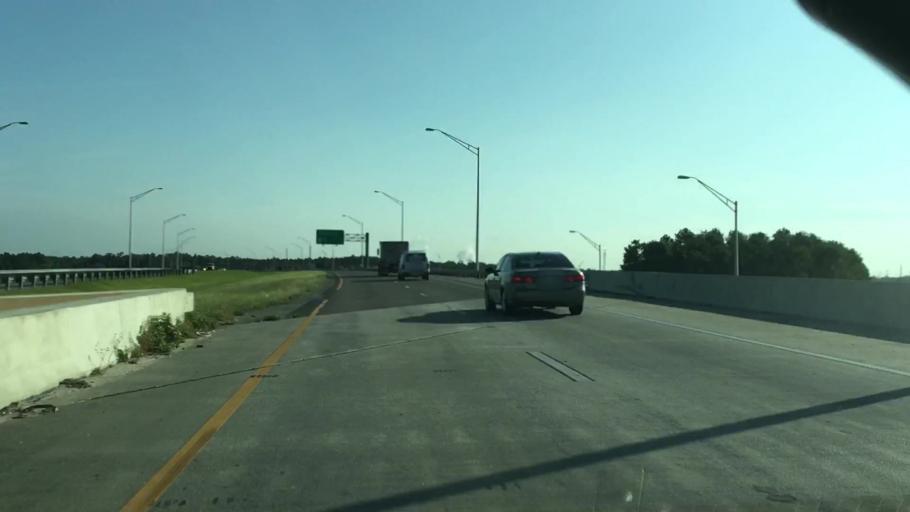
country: US
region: Florida
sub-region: Orange County
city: Taft
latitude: 28.4097
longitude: -81.2301
